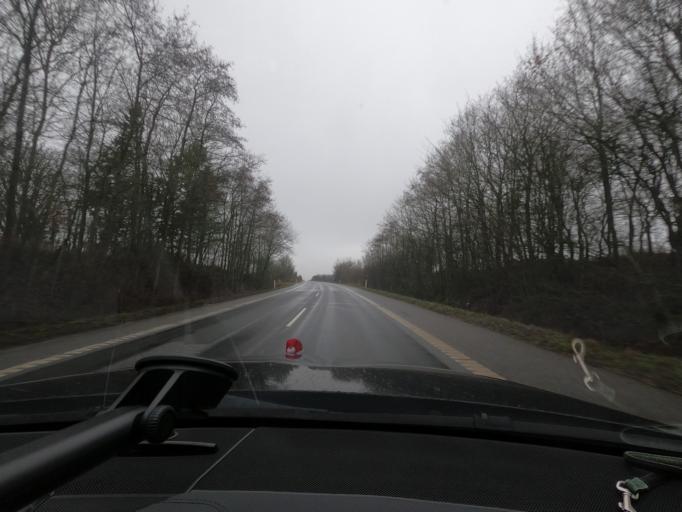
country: DK
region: South Denmark
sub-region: Sonderborg Kommune
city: Horuphav
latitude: 54.8987
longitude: 9.9592
